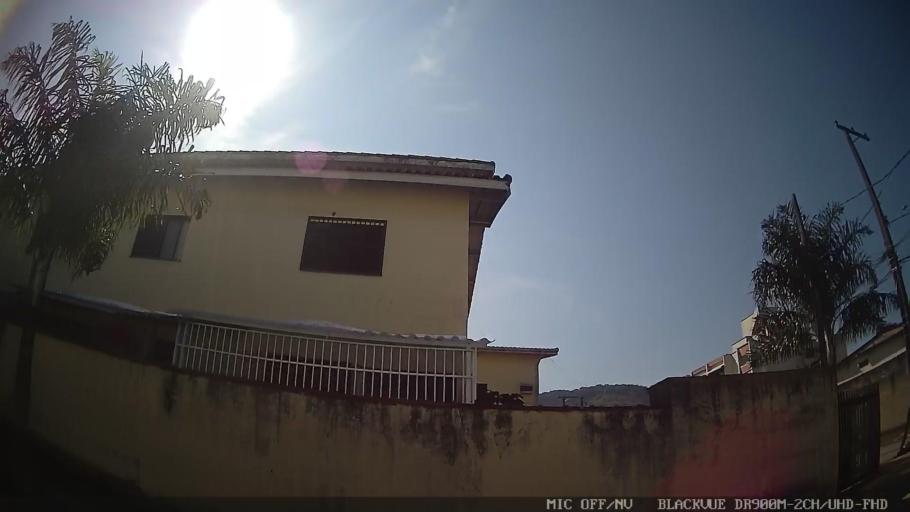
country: BR
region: Sao Paulo
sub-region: Guaruja
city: Guaruja
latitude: -24.0048
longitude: -46.2748
